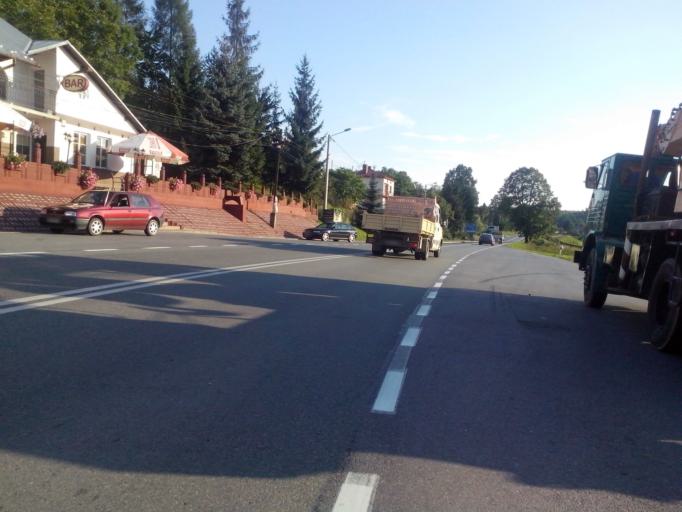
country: PL
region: Subcarpathian Voivodeship
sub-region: Powiat strzyzowski
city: Strzyzow
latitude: 49.8800
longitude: 21.8213
